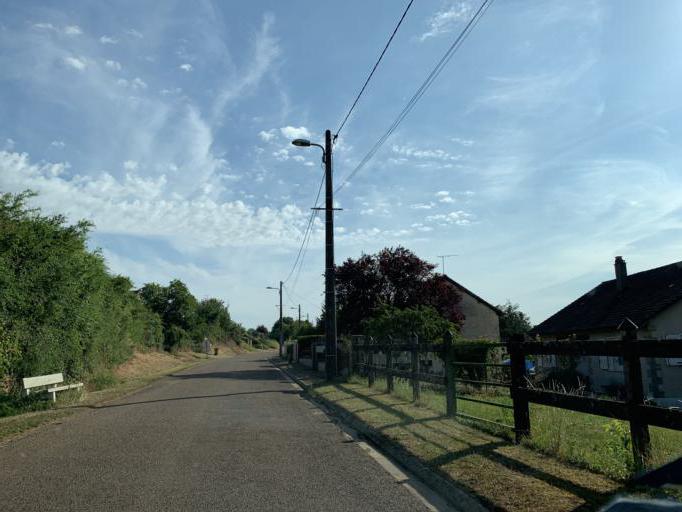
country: FR
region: Bourgogne
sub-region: Departement de la Nievre
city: Varzy
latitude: 47.4489
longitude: 3.4162
